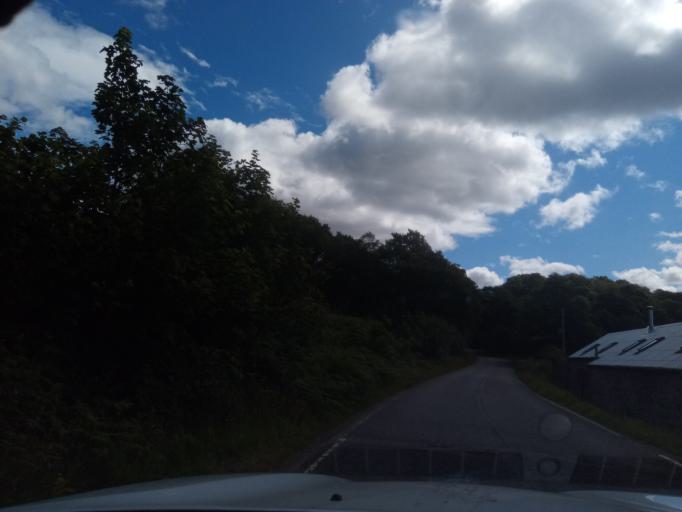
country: GB
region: Scotland
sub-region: Argyll and Bute
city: Isle Of Mull
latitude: 56.7631
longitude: -5.7477
